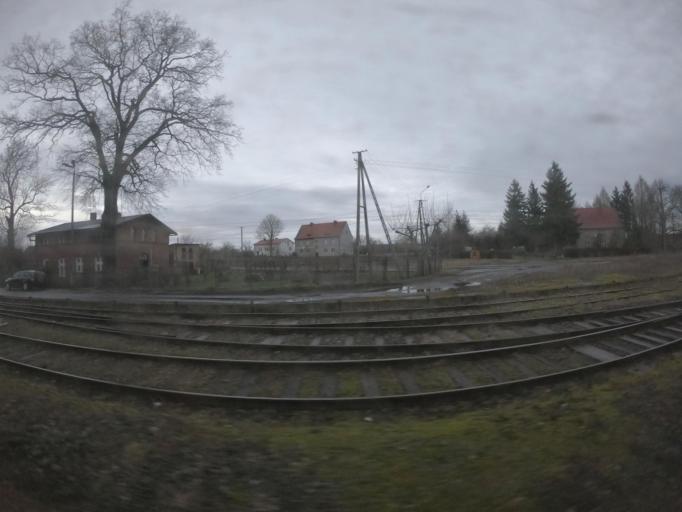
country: PL
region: West Pomeranian Voivodeship
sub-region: Powiat szczecinecki
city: Lubowo
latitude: 53.5834
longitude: 16.3883
